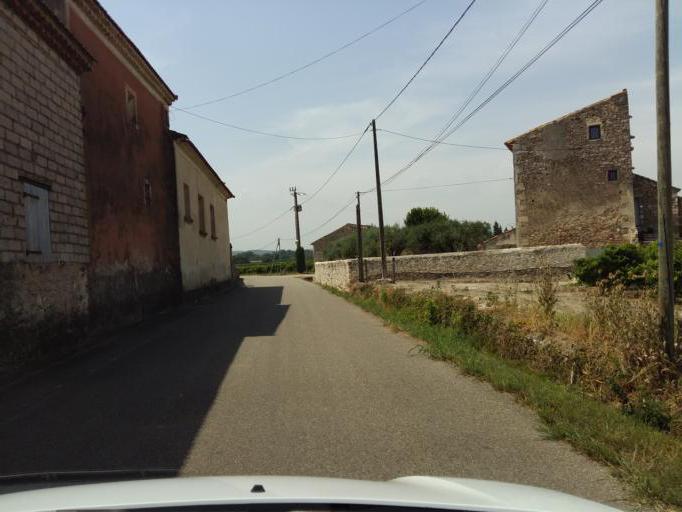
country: FR
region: Languedoc-Roussillon
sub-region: Departement du Gard
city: Pont-Saint-Esprit
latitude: 44.2681
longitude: 4.6682
